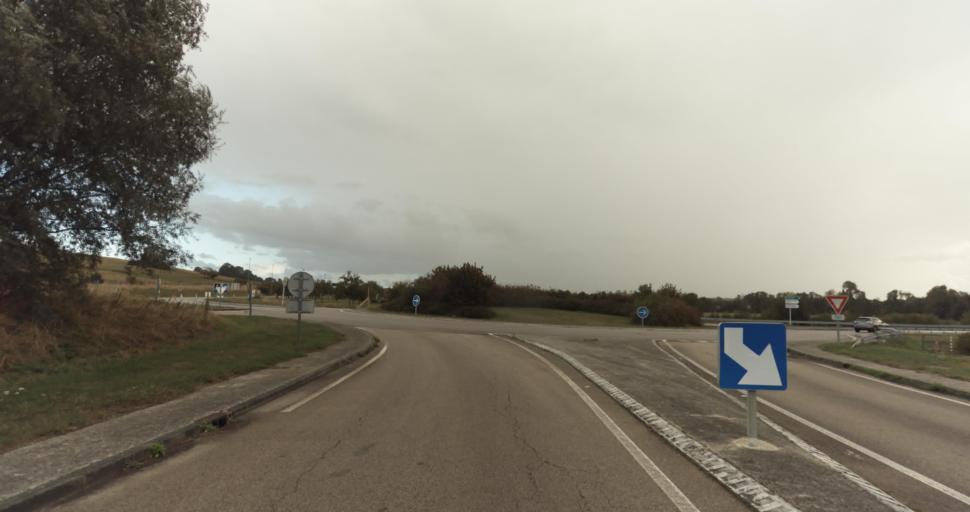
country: FR
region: Lower Normandy
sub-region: Departement de l'Orne
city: Gace
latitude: 48.7787
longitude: 0.3016
